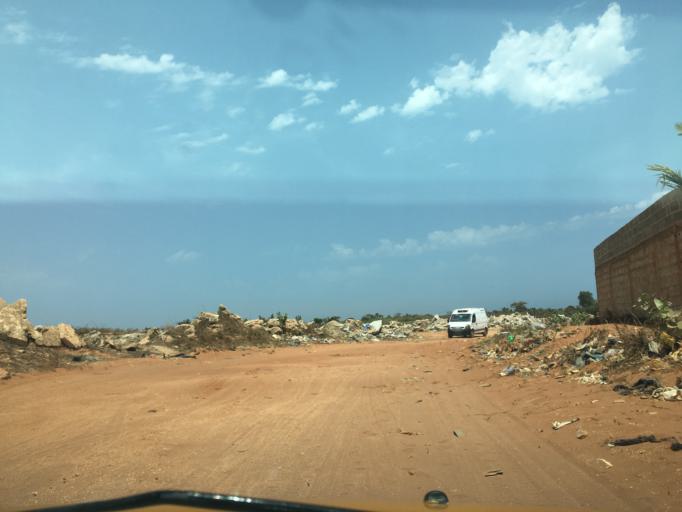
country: SN
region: Thies
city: Thies
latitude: 14.8070
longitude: -17.1894
